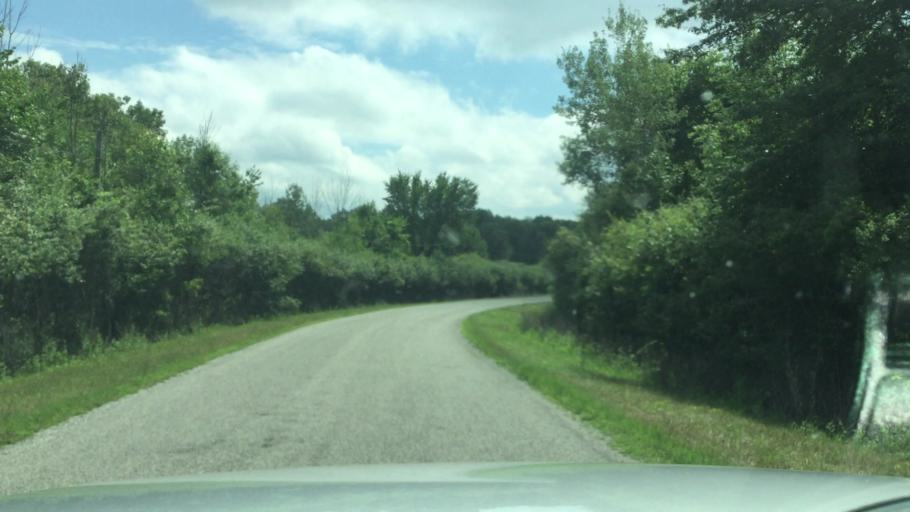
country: US
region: Michigan
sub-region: Saginaw County
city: Bridgeport
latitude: 43.3070
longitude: -83.8376
